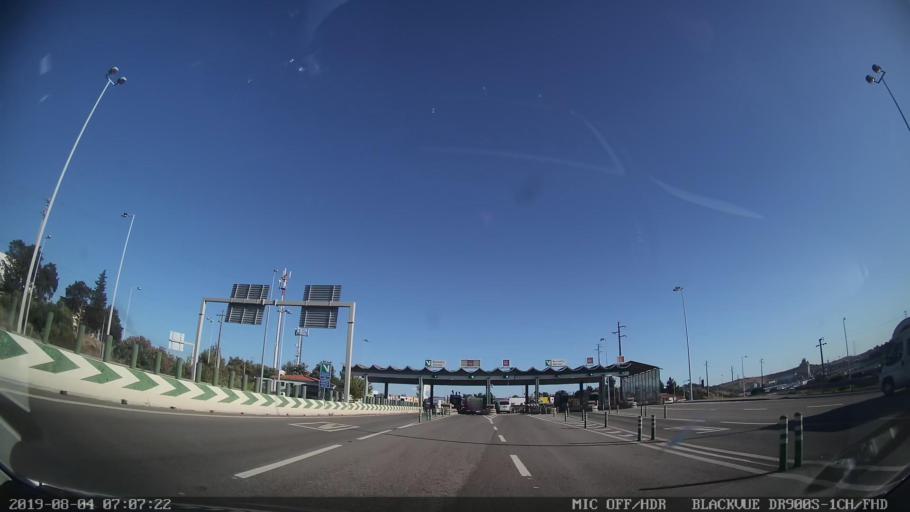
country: PT
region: Lisbon
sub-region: Vila Franca de Xira
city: Vialonga
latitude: 38.8928
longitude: -9.0482
